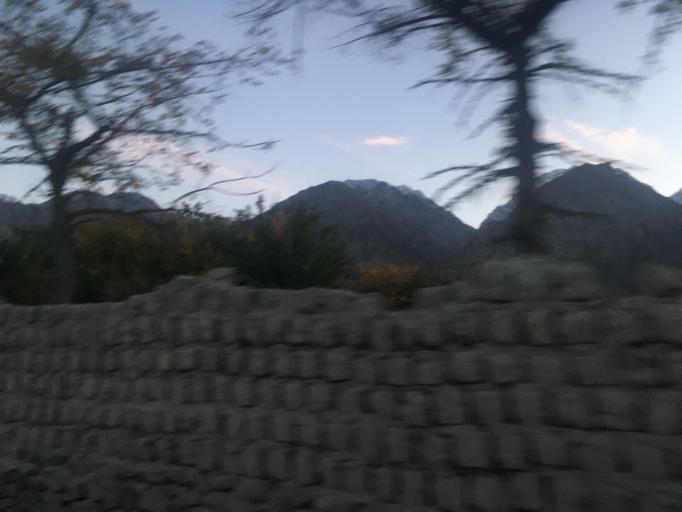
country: PK
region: Gilgit-Baltistan
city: Skardu
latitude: 35.3001
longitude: 75.5440
